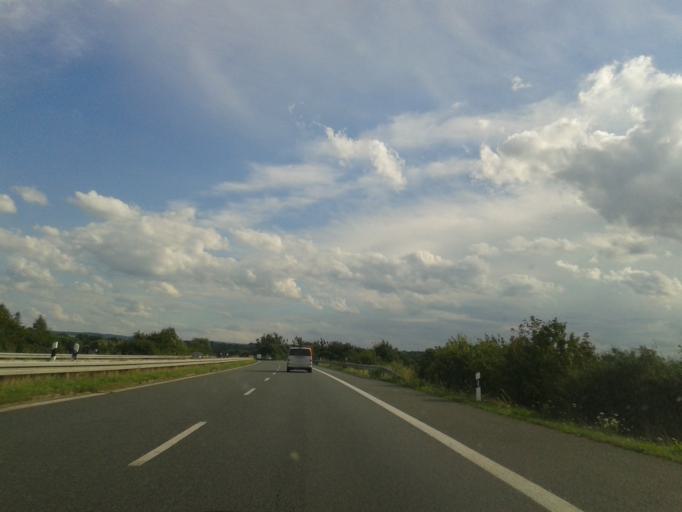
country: DE
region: Saxony
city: Pirna
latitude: 50.9773
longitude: 13.9156
